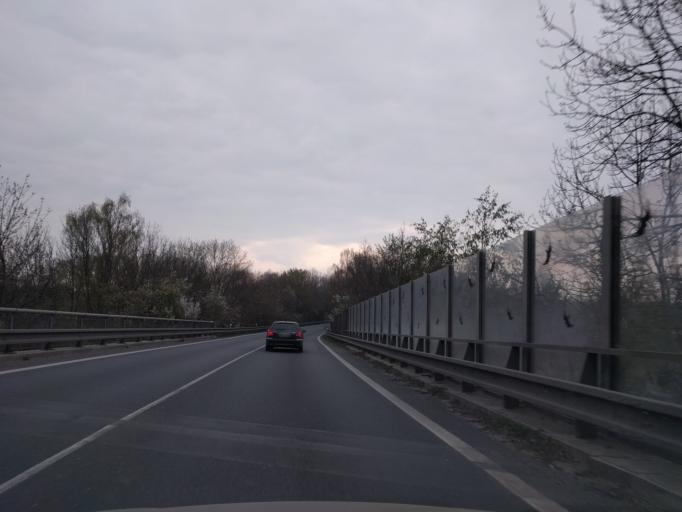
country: CZ
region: Central Bohemia
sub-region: Okres Praha-Vychod
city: Ricany
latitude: 49.9799
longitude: 14.6356
